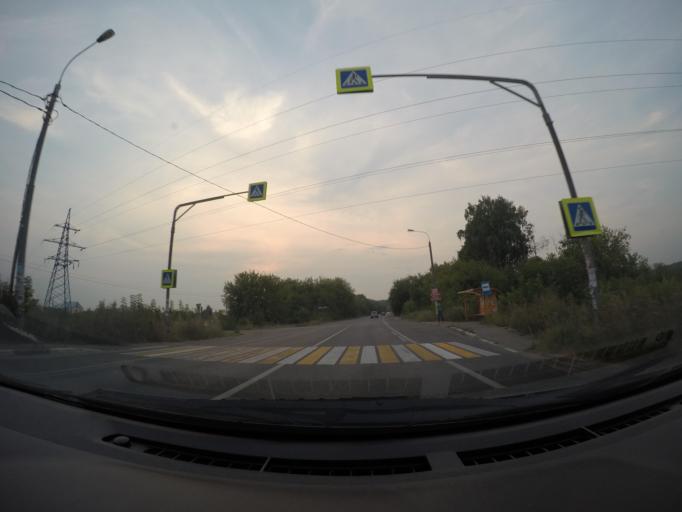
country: RU
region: Moskovskaya
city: Rechitsy
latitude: 55.5858
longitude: 38.5415
